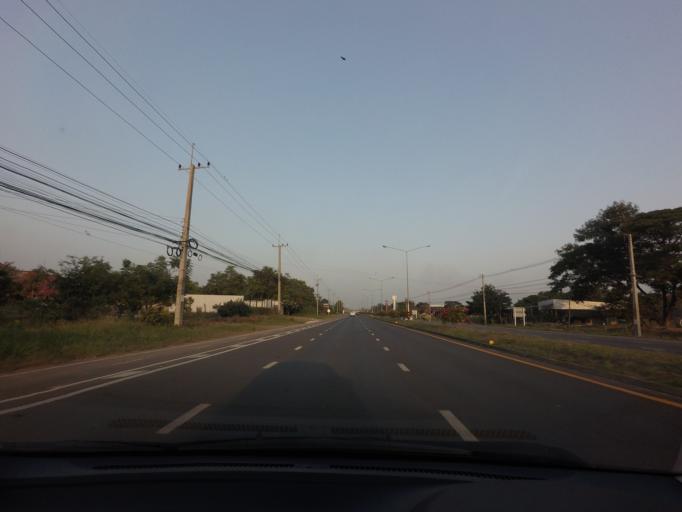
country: TH
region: Sukhothai
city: Sukhothai
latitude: 17.0212
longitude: 99.8650
